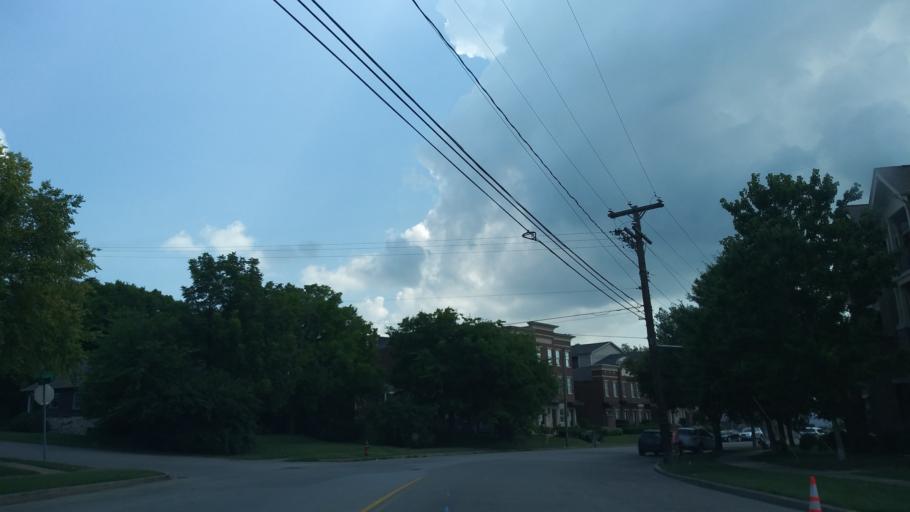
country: US
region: Tennessee
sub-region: Davidson County
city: Nashville
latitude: 36.1455
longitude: -86.8195
